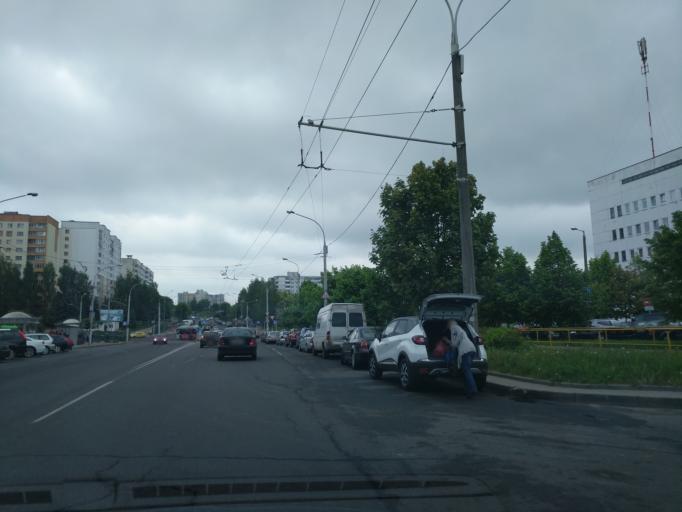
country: BY
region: Minsk
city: Novoye Medvezhino
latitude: 53.8976
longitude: 27.4528
